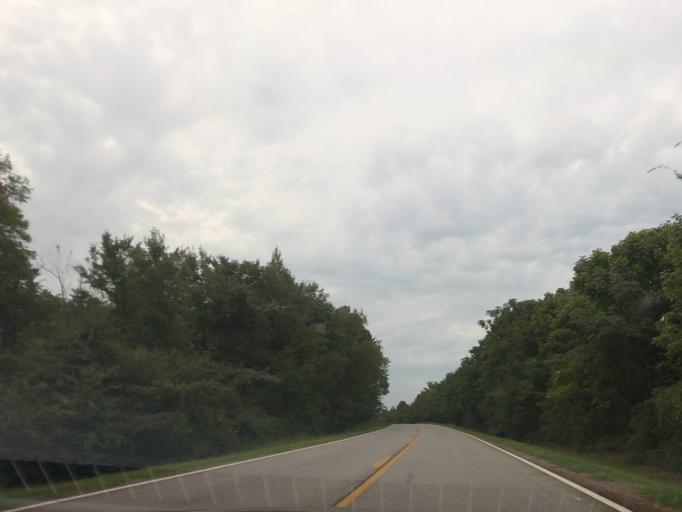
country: US
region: Georgia
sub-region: Twiggs County
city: Jeffersonville
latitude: 32.7323
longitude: -83.4194
